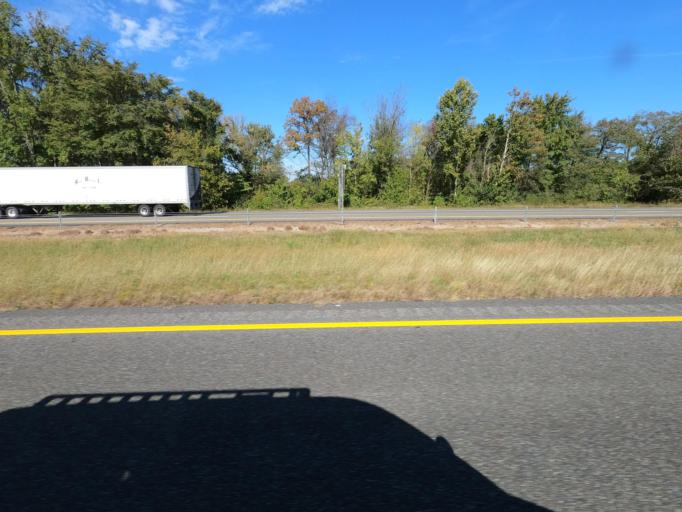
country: US
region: Tennessee
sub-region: Haywood County
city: Brownsville
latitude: 35.4662
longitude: -89.2925
